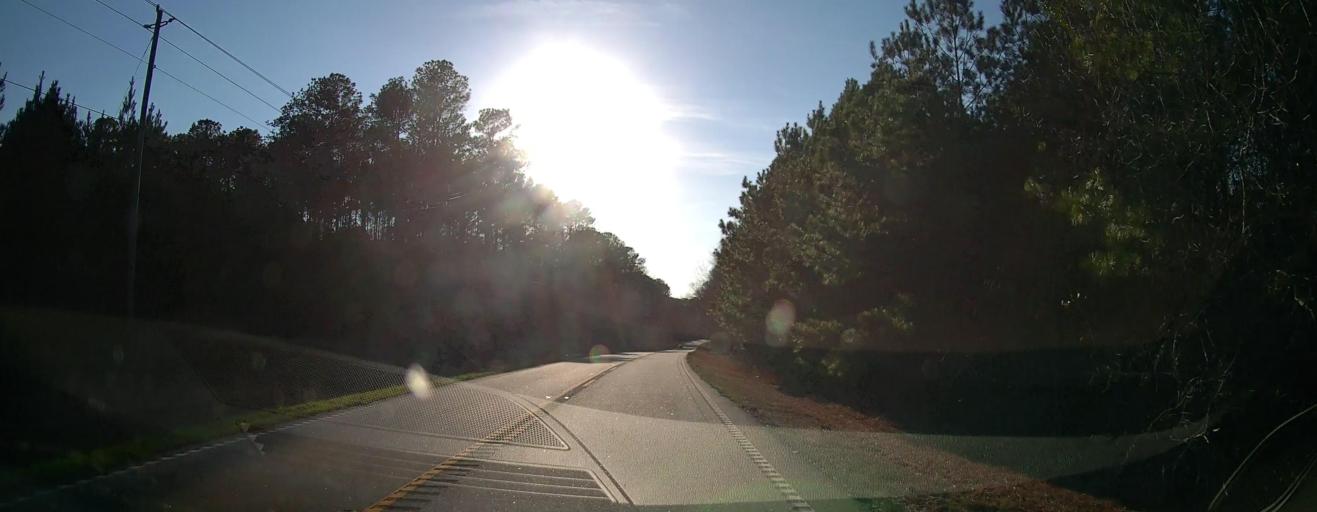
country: US
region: Alabama
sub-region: Chambers County
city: Valley
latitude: 32.7420
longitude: -85.0570
